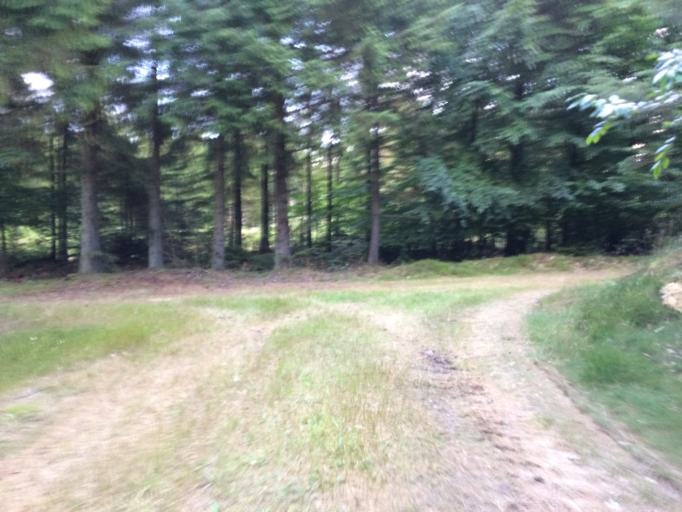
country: DK
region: Central Jutland
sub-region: Holstebro Kommune
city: Ulfborg
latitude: 56.2599
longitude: 8.3764
